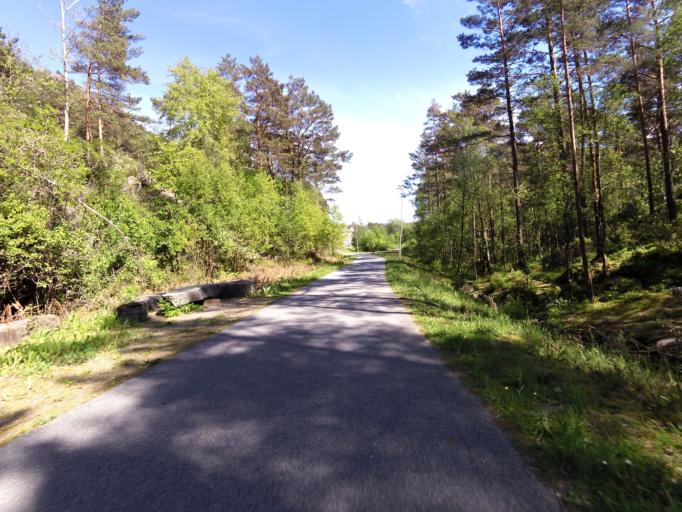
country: NO
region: Hordaland
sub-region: Stord
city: Sagvag
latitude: 59.7818
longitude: 5.3815
